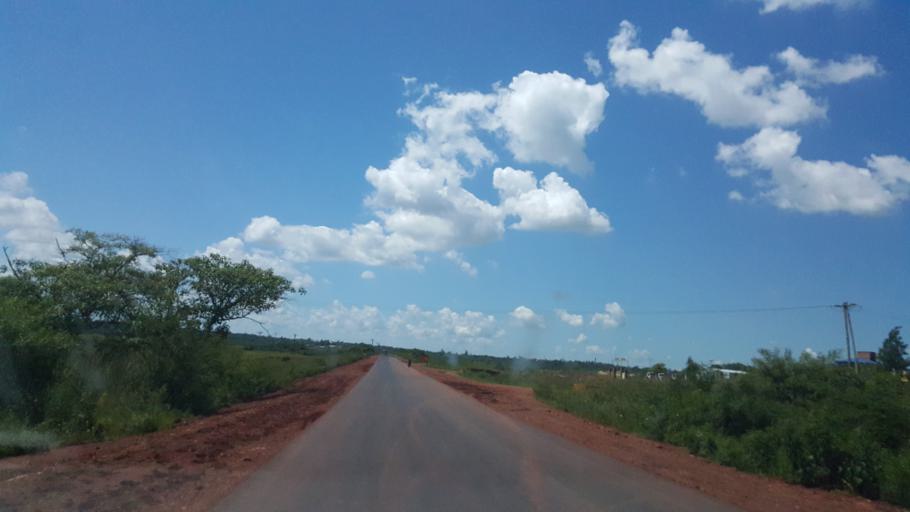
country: AR
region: Corrientes
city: Santo Tome
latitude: -28.5251
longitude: -56.0552
